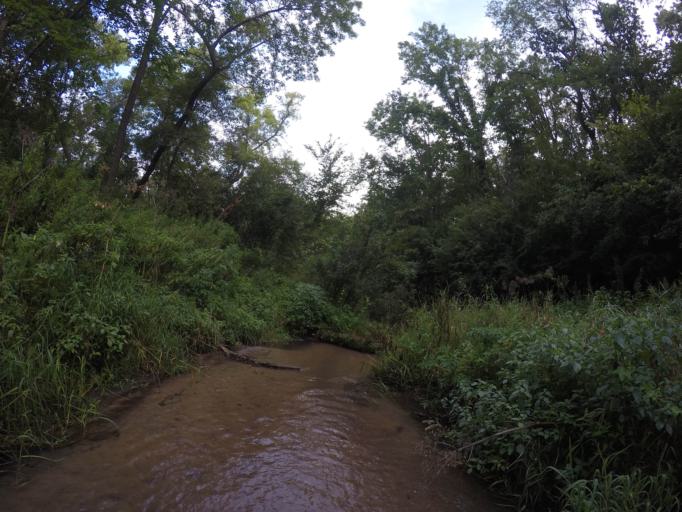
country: US
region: Minnesota
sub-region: Olmsted County
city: Eyota
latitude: 43.9804
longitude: -92.3358
